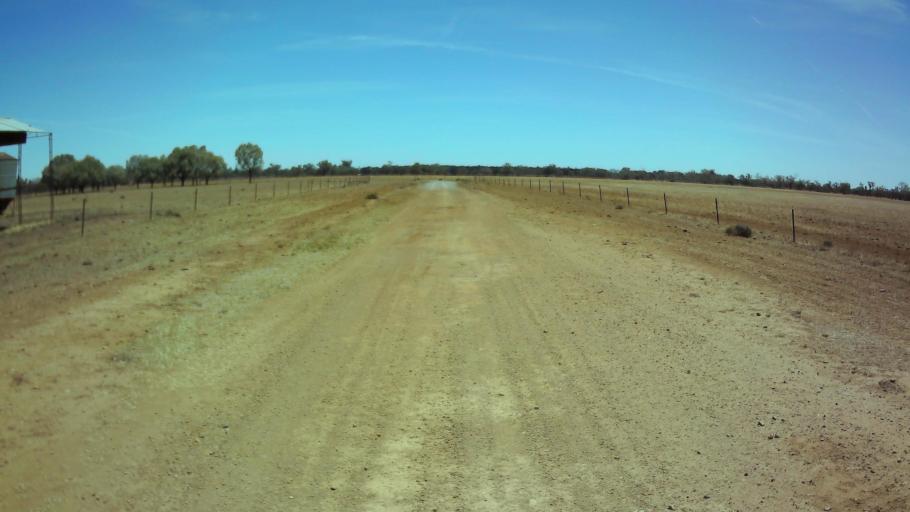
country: AU
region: New South Wales
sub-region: Bland
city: West Wyalong
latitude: -33.8278
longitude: 147.6383
